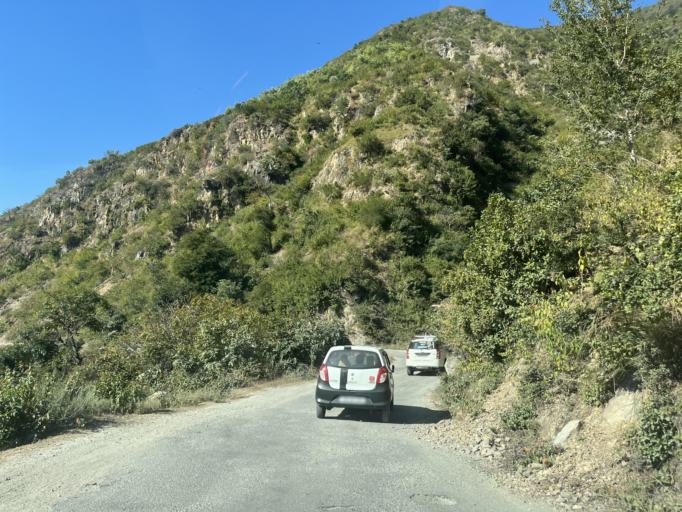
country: IN
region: Uttarakhand
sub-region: Naini Tal
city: Naini Tal
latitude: 29.5111
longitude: 79.4679
